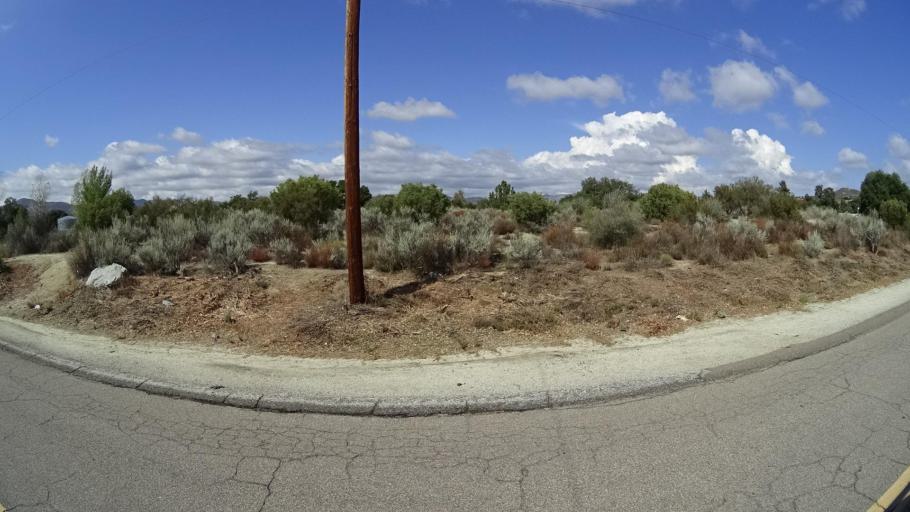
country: US
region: California
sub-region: San Diego County
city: Campo
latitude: 32.6792
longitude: -116.5064
